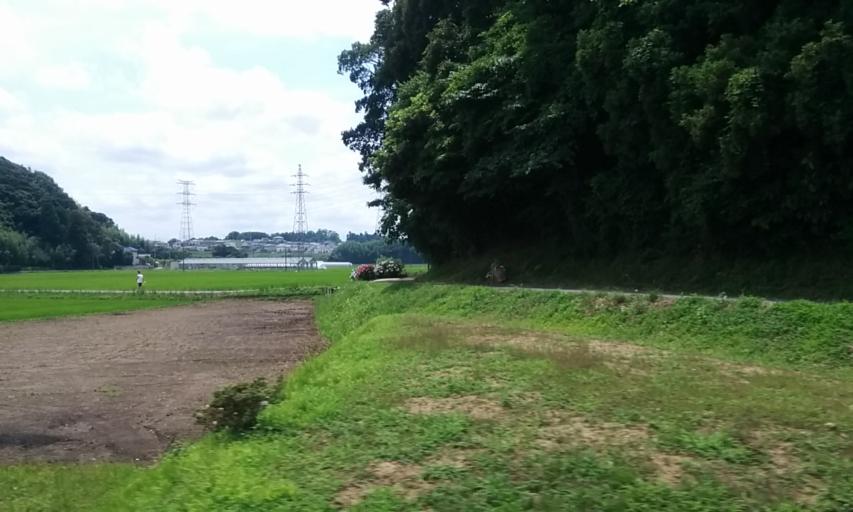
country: JP
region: Chiba
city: Katori-shi
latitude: 35.8928
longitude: 140.4037
